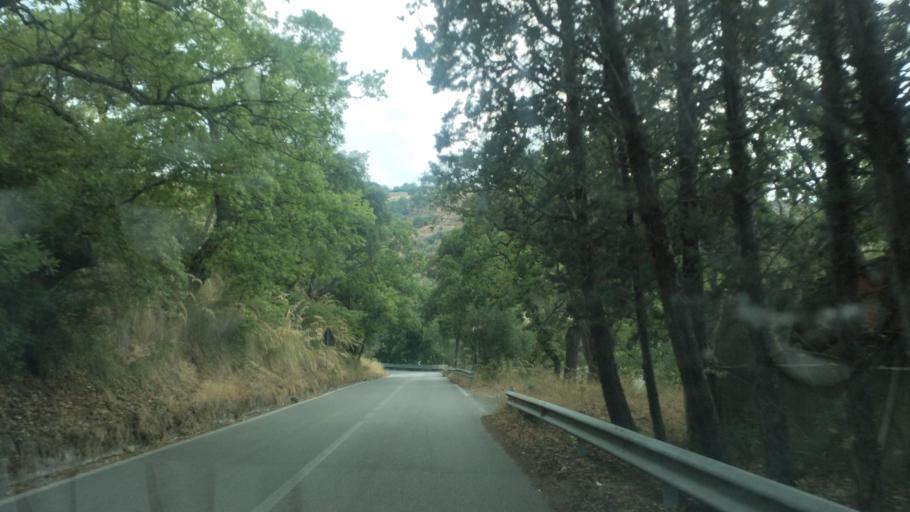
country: IT
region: Calabria
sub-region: Provincia di Catanzaro
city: Squillace Lido
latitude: 38.7603
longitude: 16.5652
